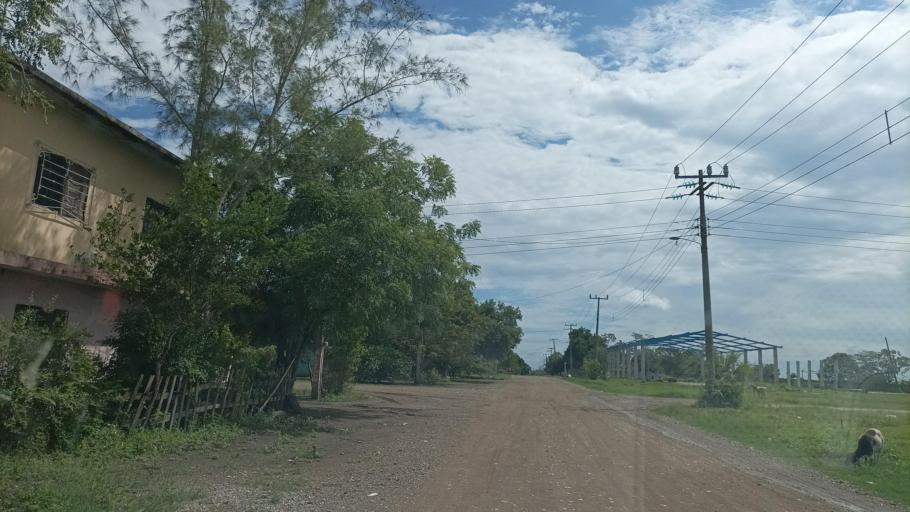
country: MX
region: Veracruz
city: Panuco
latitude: 21.9489
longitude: -98.1368
